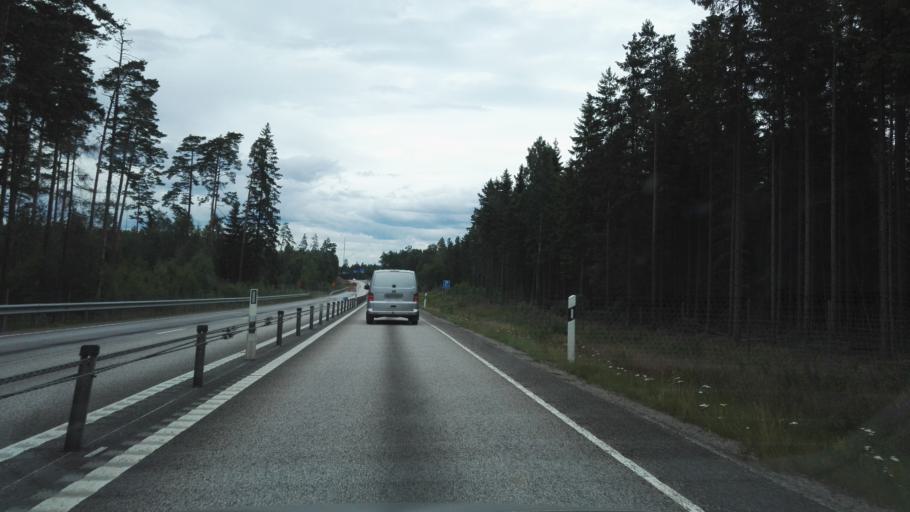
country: SE
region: Kronoberg
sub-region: Vaxjo Kommun
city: Braas
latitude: 57.0117
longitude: 15.0486
